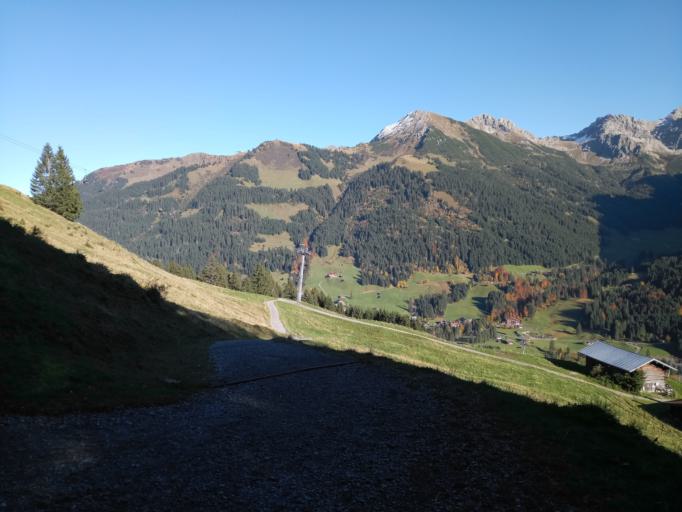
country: AT
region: Vorarlberg
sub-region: Politischer Bezirk Bregenz
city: Mittelberg
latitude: 47.3280
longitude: 10.1505
